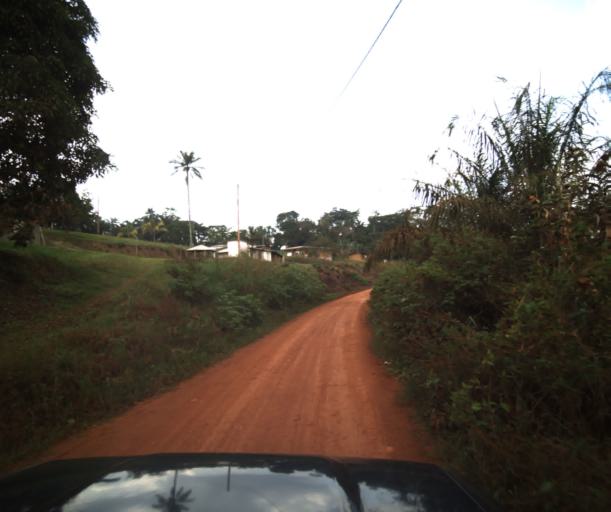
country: CM
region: Centre
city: Akono
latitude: 3.6032
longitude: 11.1866
